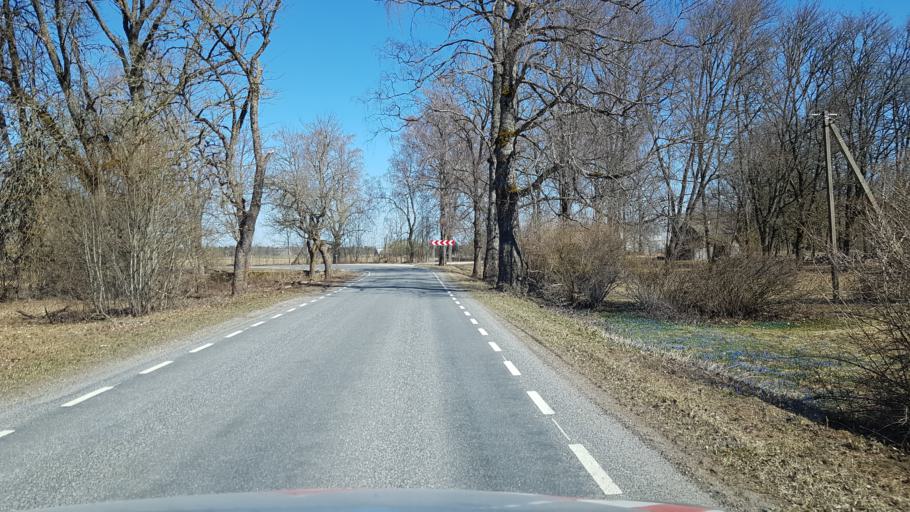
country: EE
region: Laeaene-Virumaa
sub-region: Vinni vald
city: Vinni
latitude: 59.0987
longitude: 26.5253
